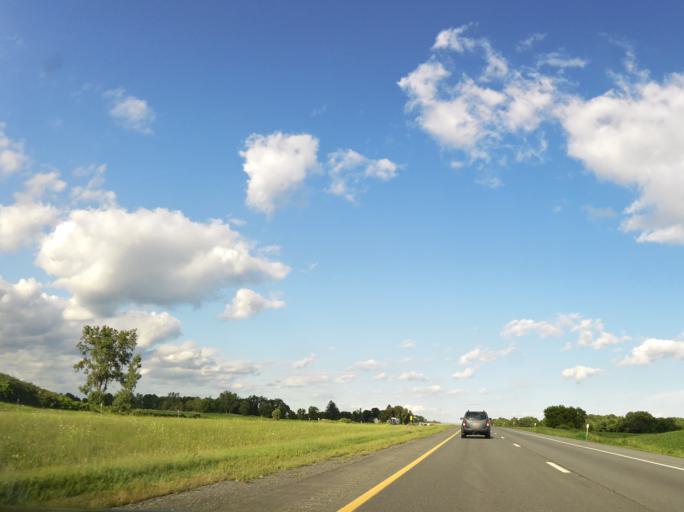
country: US
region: New York
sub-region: Genesee County
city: Batavia
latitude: 43.0173
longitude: -78.2272
